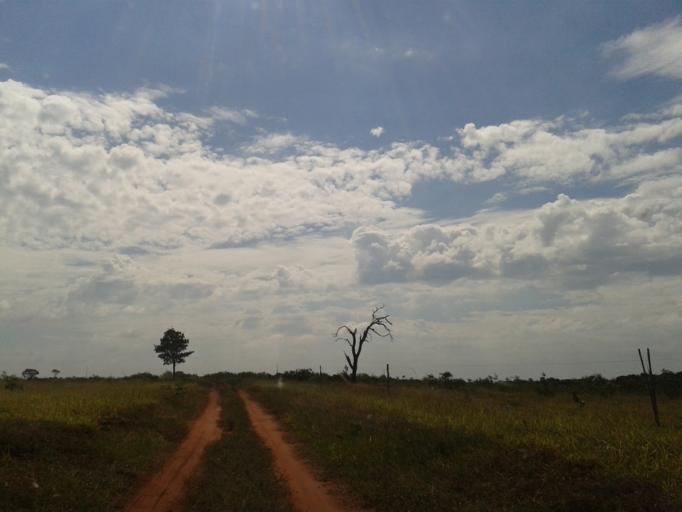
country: BR
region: Minas Gerais
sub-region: Campina Verde
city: Campina Verde
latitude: -19.3828
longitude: -49.6674
